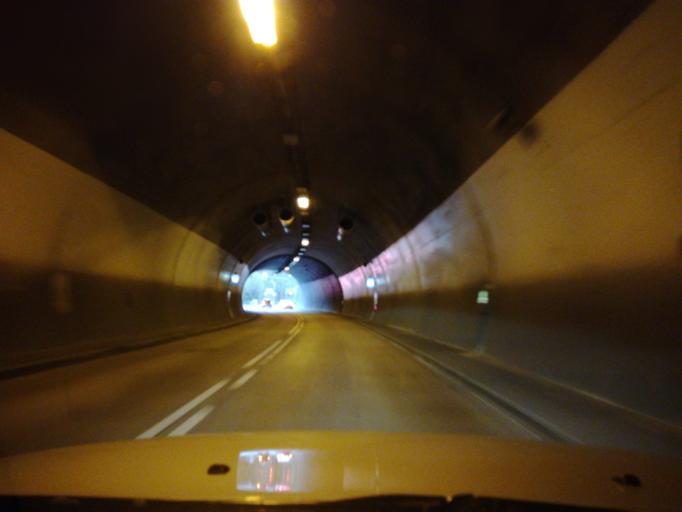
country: DE
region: North Rhine-Westphalia
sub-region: Regierungsbezirk Dusseldorf
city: Velbert
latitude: 51.3491
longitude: 7.1218
